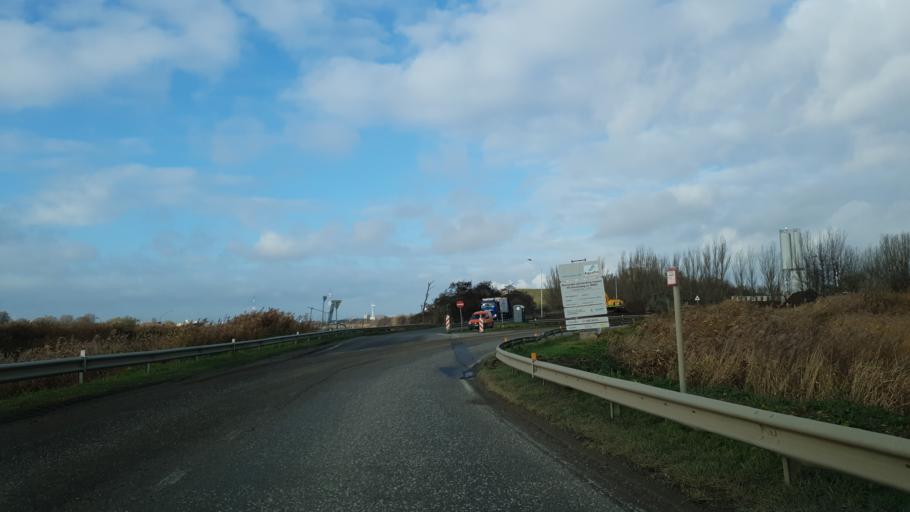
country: BE
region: Flanders
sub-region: Provincie Antwerpen
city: Stabroek
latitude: 51.3037
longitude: 4.3628
